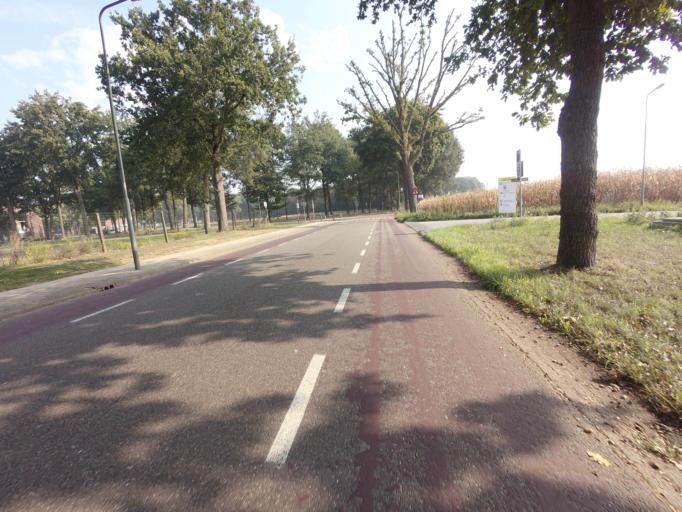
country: NL
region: Limburg
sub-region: Gemeente Maasgouw
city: Maasbracht
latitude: 51.1441
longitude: 5.8956
